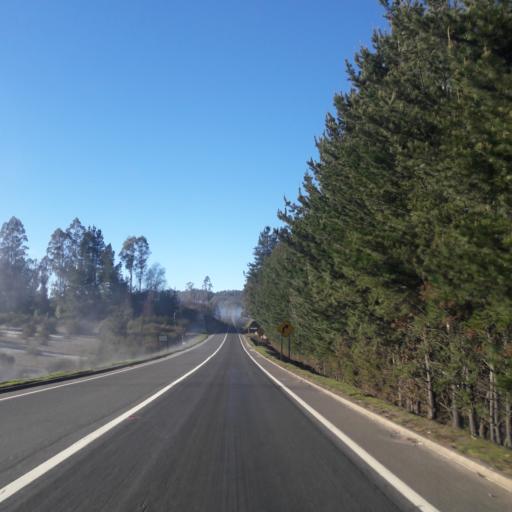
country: CL
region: Biobio
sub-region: Provincia de Biobio
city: La Laja
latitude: -37.2846
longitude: -72.9399
